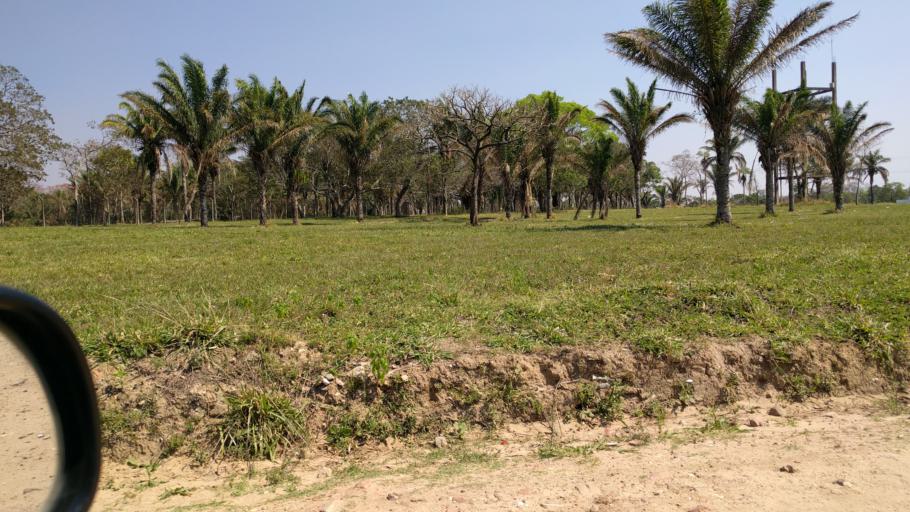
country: BO
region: Santa Cruz
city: Santa Cruz de la Sierra
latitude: -17.7541
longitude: -63.2304
